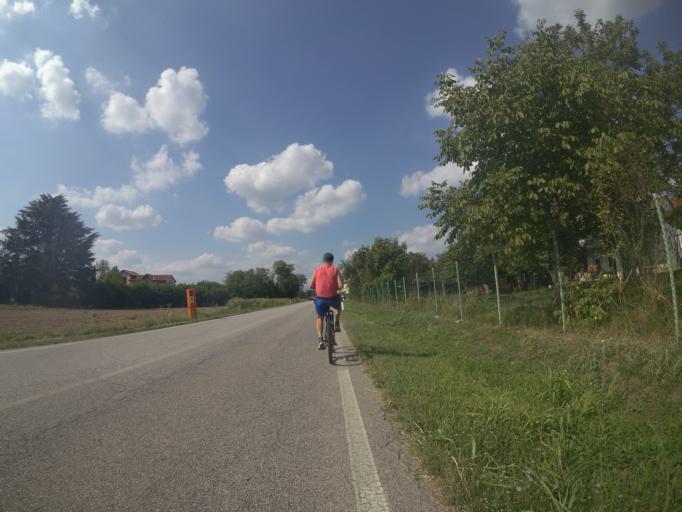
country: IT
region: Friuli Venezia Giulia
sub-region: Provincia di Udine
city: Basiliano-Vissandone
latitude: 46.0405
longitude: 13.0993
